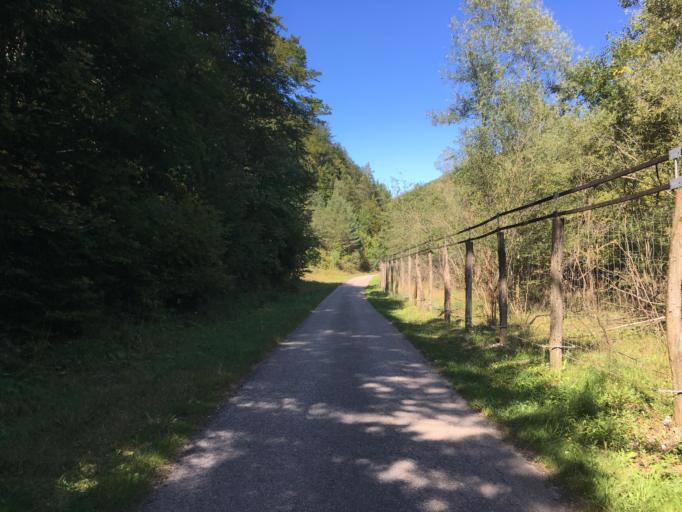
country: SK
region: Trenciansky
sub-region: Okres Povazska Bystrica
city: Povazska Bystrica
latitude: 49.0212
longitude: 18.4385
